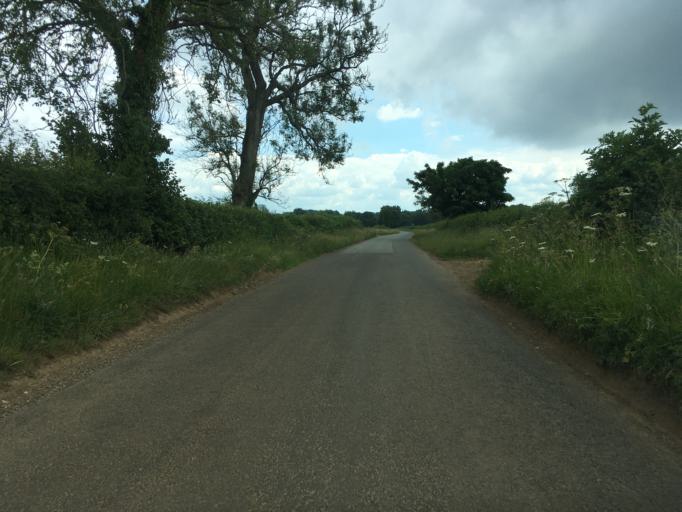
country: GB
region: England
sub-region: Gloucestershire
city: Coates
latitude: 51.7607
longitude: -2.0614
